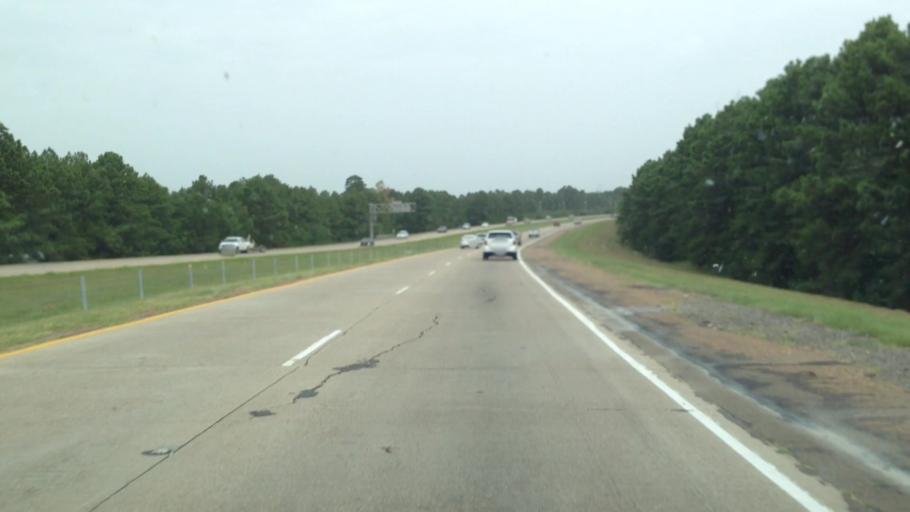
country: US
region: Louisiana
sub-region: Caddo Parish
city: Shreveport
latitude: 32.4209
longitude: -93.8327
